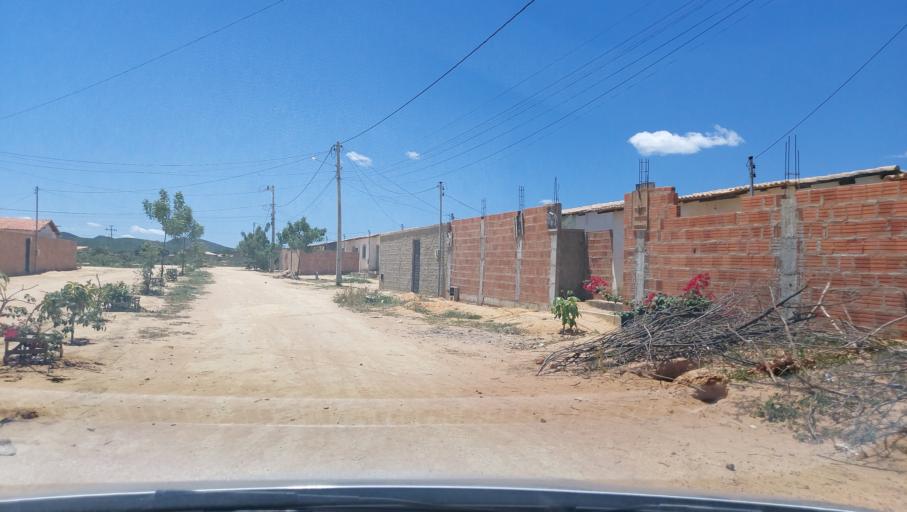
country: BR
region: Bahia
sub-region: Oliveira Dos Brejinhos
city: Beira Rio
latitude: -12.0031
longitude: -42.6338
